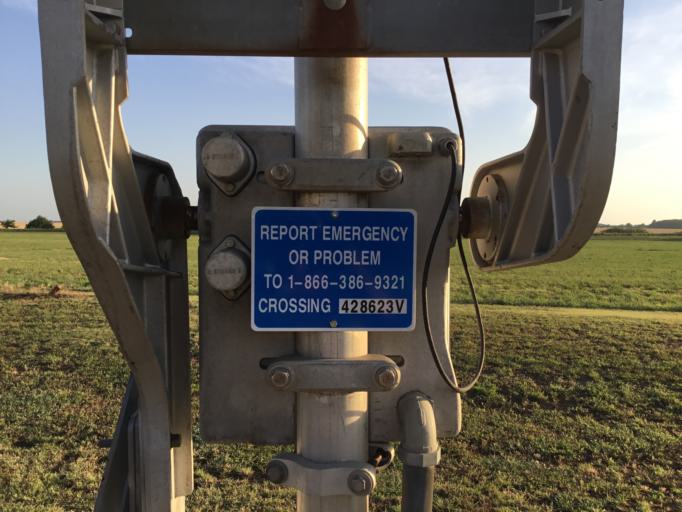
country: US
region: Kansas
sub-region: Sedgwick County
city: Cheney
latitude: 37.4592
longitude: -97.8594
